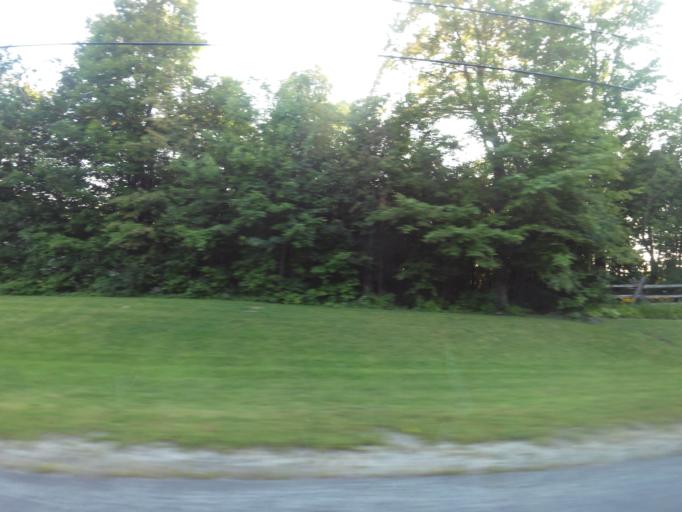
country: CA
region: Ontario
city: Clarence-Rockland
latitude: 45.5034
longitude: -75.4304
